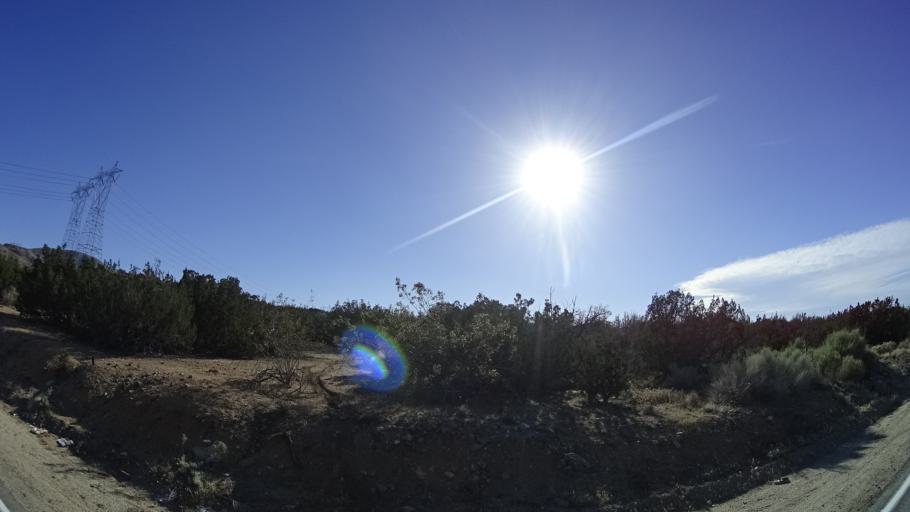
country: US
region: California
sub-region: Los Angeles County
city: Littlerock
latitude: 34.5105
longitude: -118.0297
